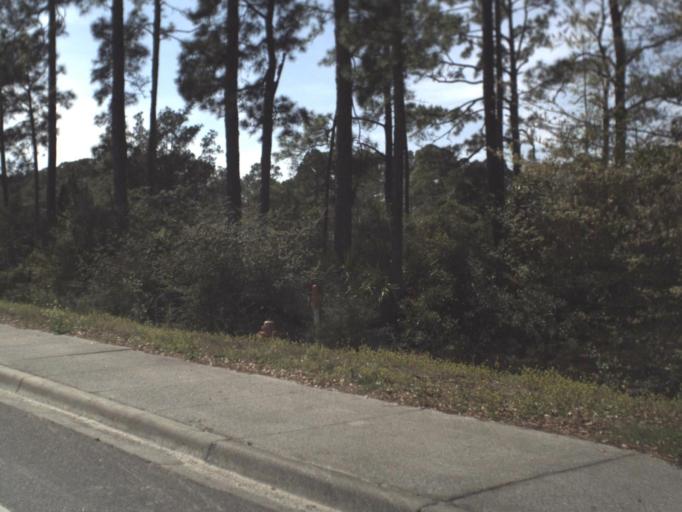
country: US
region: Florida
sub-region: Bay County
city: Lynn Haven
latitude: 30.2674
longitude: -85.6440
